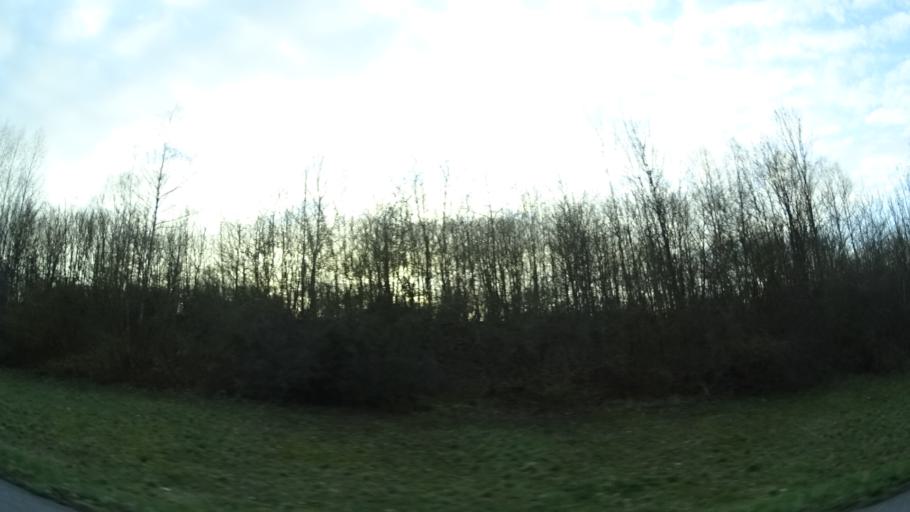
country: DE
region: Rheinland-Pfalz
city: Gumbsheim
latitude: 49.8383
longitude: 7.9936
